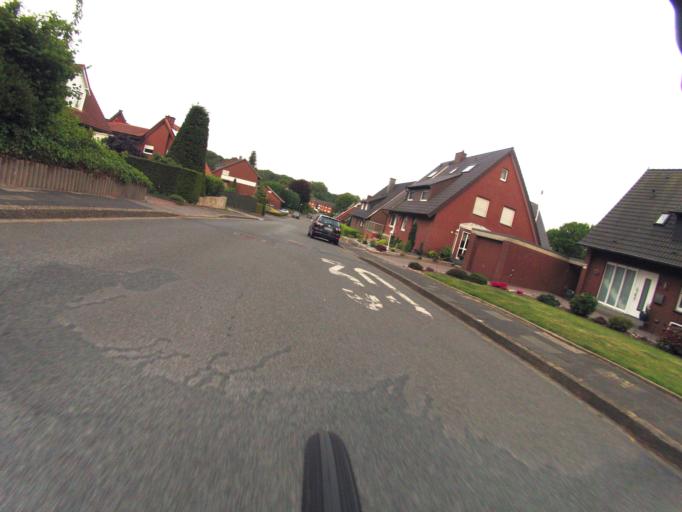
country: DE
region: North Rhine-Westphalia
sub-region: Regierungsbezirk Munster
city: Mettingen
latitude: 52.2744
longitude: 7.7745
